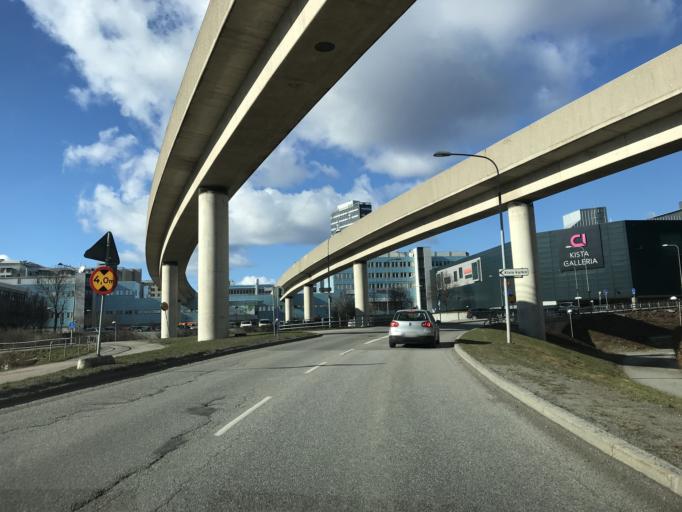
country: SE
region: Stockholm
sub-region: Stockholms Kommun
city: Kista
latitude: 59.4008
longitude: 17.9455
